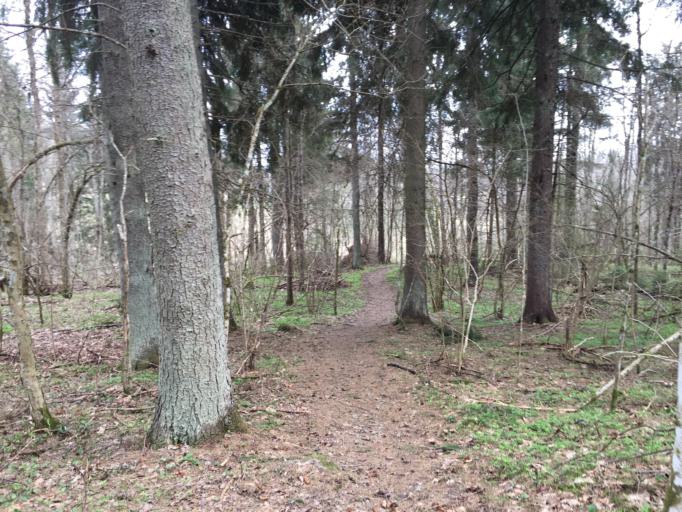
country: EE
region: Vorumaa
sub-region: Voru linn
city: Voru
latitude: 57.7136
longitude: 27.0618
